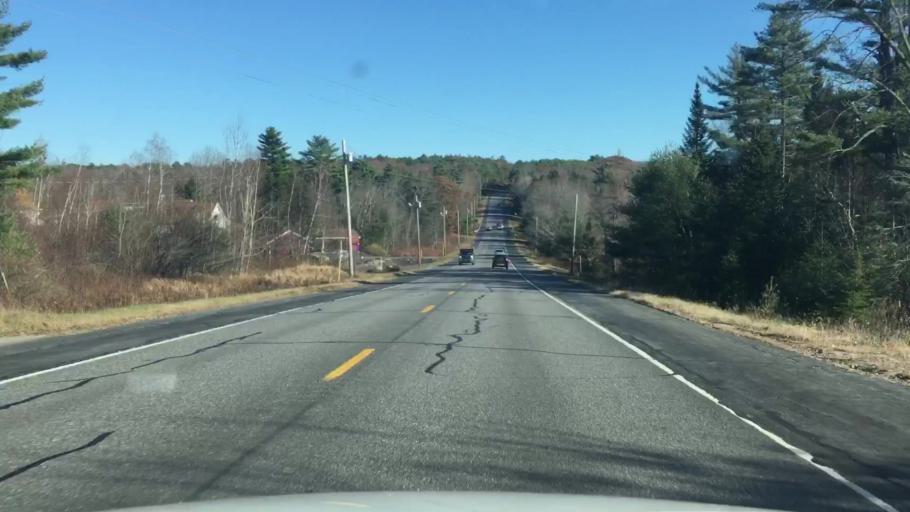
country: US
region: Maine
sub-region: Knox County
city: Union
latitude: 44.2139
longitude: -69.2430
